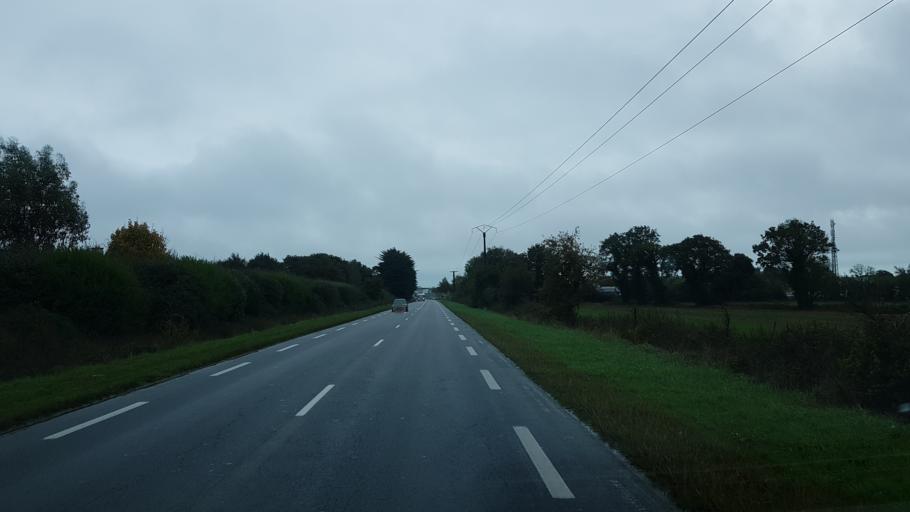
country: FR
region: Brittany
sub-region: Departement du Morbihan
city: Sarzeau
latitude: 47.5241
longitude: -2.7879
